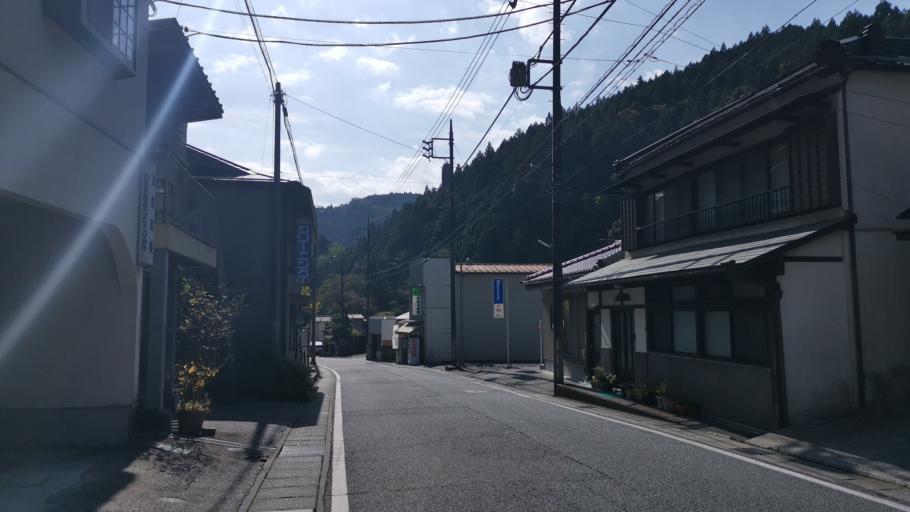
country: JP
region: Shizuoka
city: Fujinomiya
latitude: 35.3721
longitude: 138.4250
